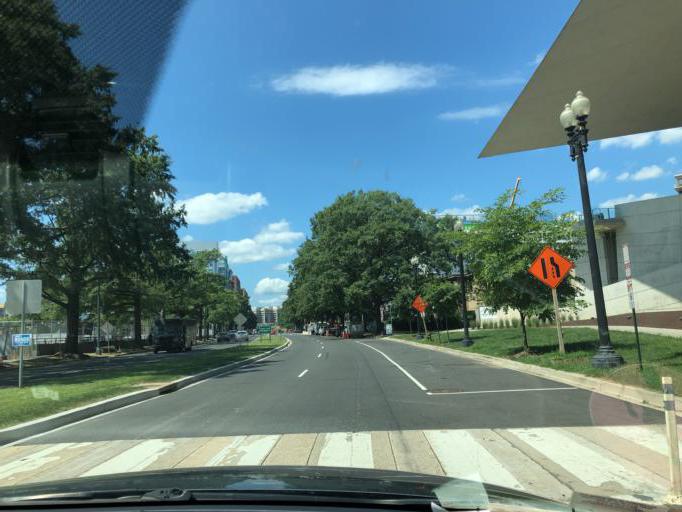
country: US
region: Washington, D.C.
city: Washington, D.C.
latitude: 38.8773
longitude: -77.0210
